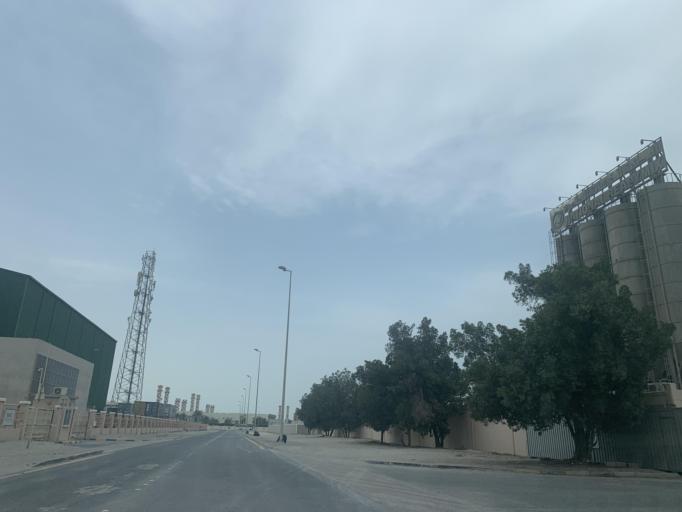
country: BH
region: Muharraq
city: Al Hadd
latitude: 26.2084
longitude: 50.6622
